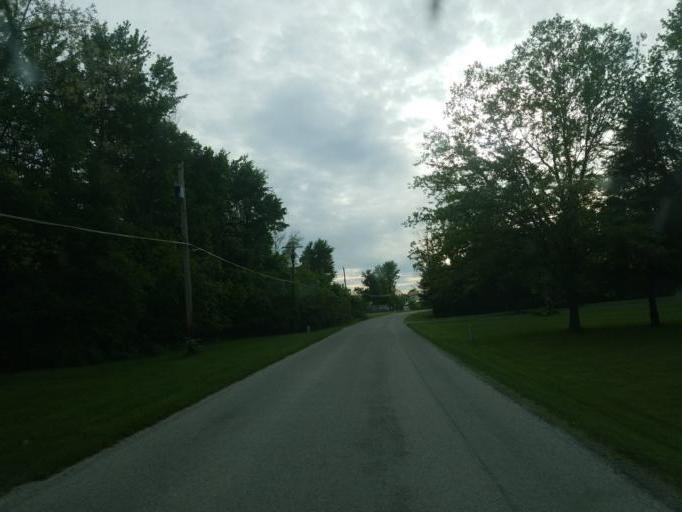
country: US
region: Ohio
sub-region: Richland County
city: Ontario
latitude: 40.8146
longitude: -82.5989
